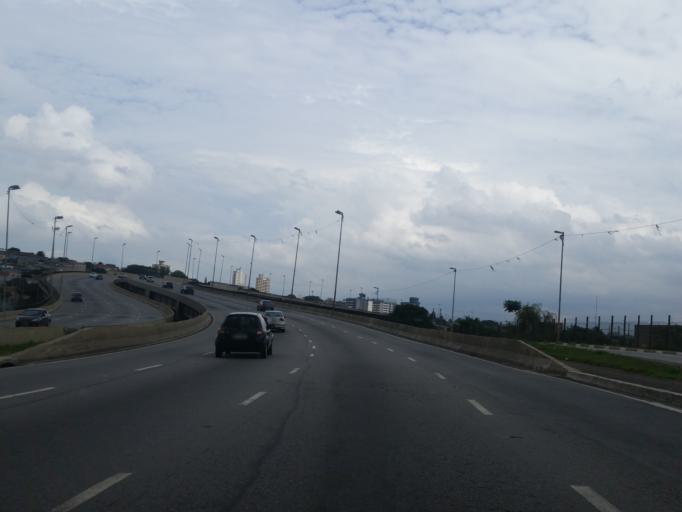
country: BR
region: Sao Paulo
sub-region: Guarulhos
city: Guarulhos
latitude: -23.4892
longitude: -46.4535
